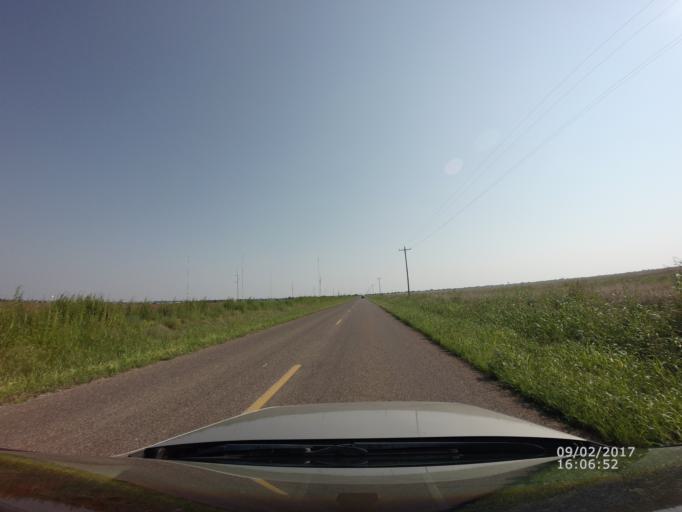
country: US
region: New Mexico
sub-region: Curry County
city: Clovis
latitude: 34.4465
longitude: -103.2141
